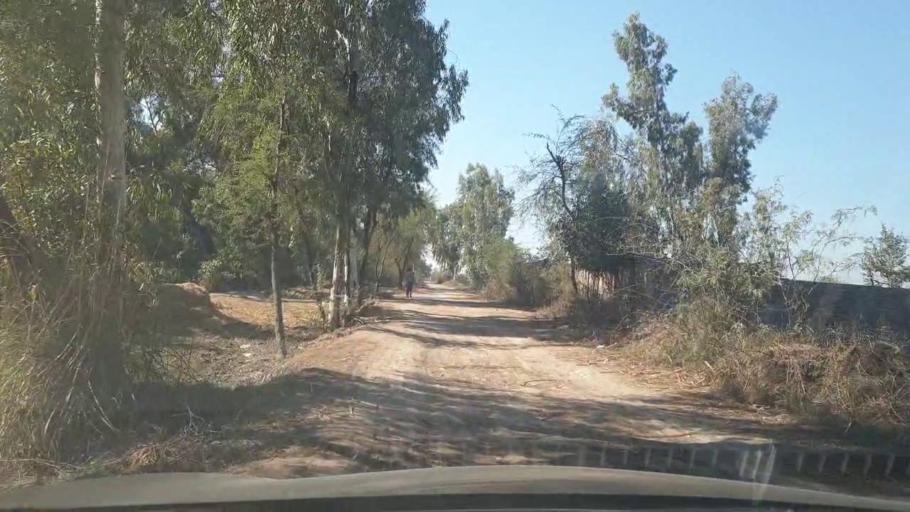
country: PK
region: Sindh
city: Mirpur Mathelo
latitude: 28.0613
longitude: 69.5010
